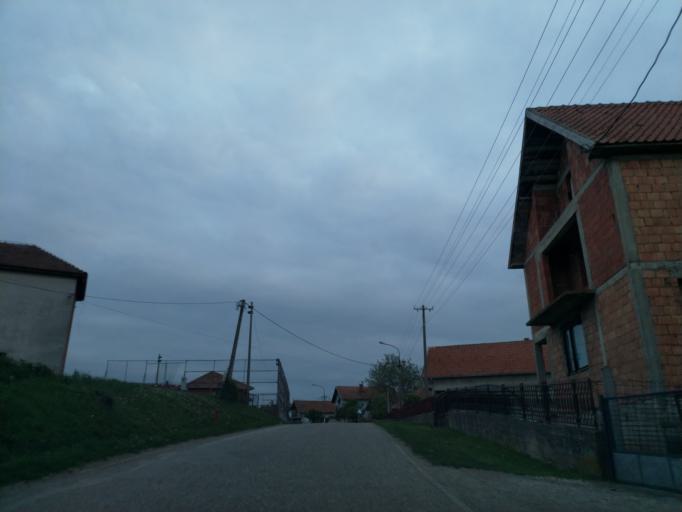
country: RS
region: Central Serbia
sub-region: Pomoravski Okrug
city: Paracin
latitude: 43.9416
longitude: 21.4947
